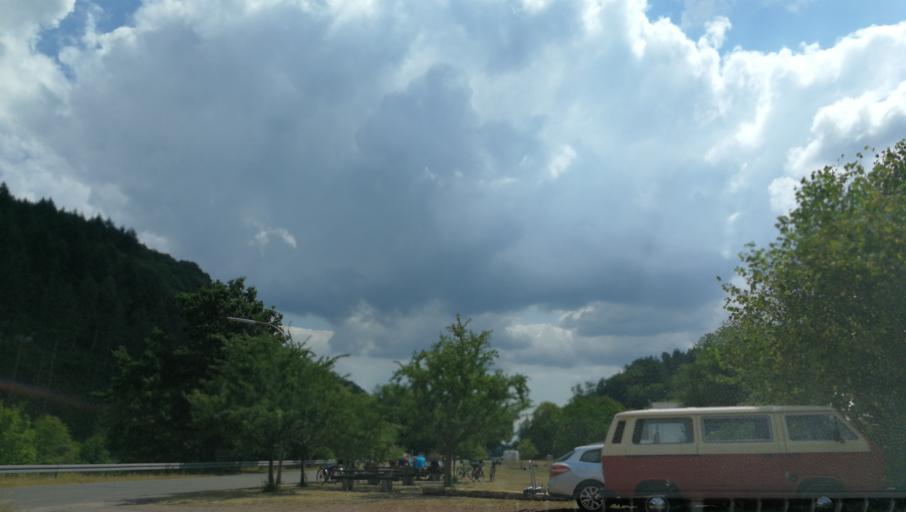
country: DE
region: Saarland
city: Mettlach
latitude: 49.4873
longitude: 6.5649
